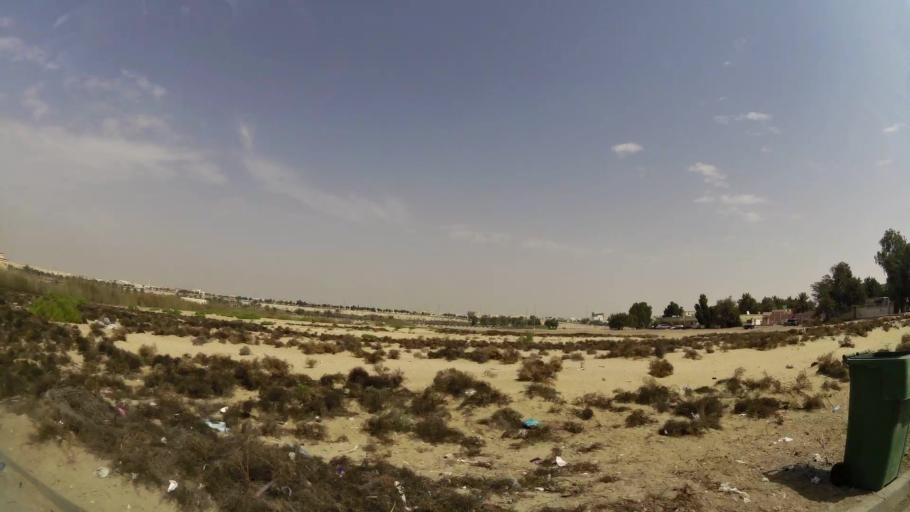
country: AE
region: Abu Dhabi
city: Abu Dhabi
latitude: 24.3009
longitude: 54.6313
